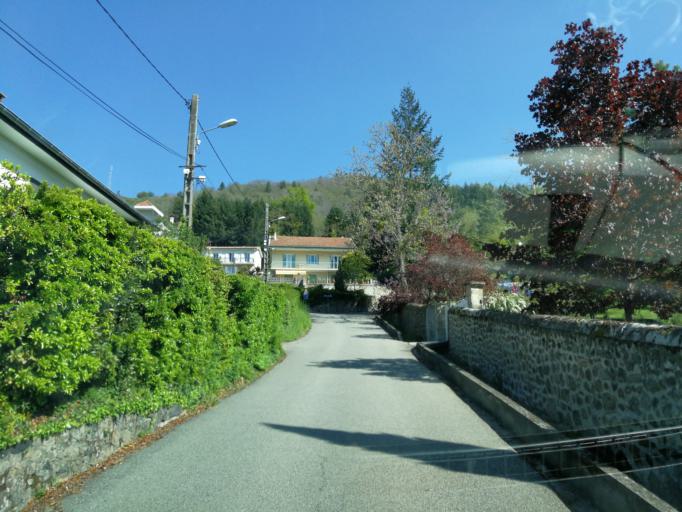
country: FR
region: Rhone-Alpes
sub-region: Departement de l'Ardeche
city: Le Cheylard
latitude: 44.9138
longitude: 4.4268
